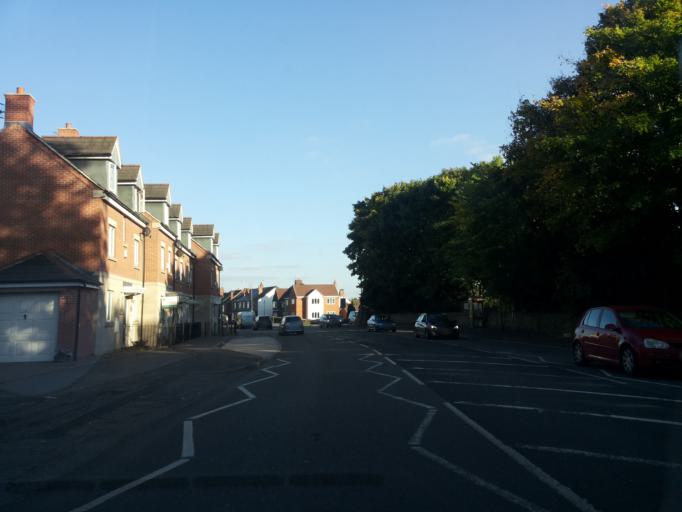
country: GB
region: England
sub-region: Derbyshire
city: Wingerworth
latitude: 53.2313
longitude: -1.4714
